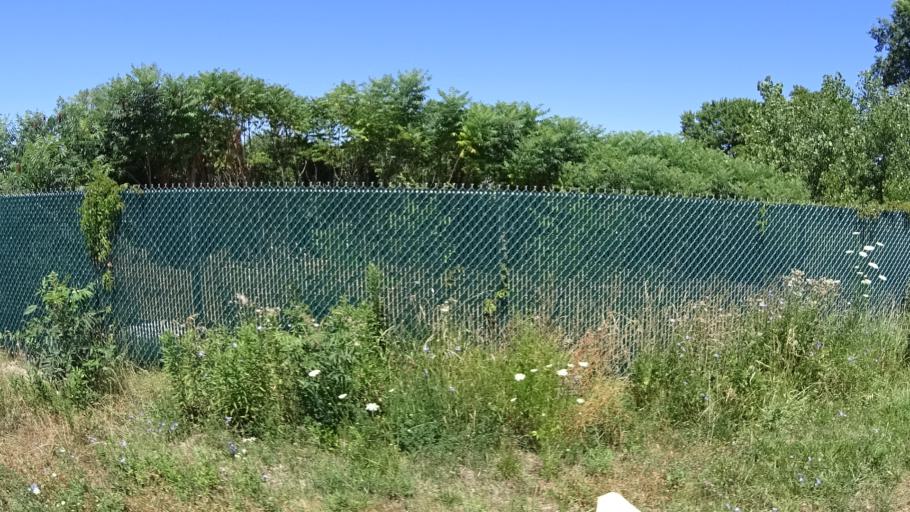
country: US
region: Ohio
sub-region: Erie County
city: Sandusky
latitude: 41.4498
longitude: -82.6861
